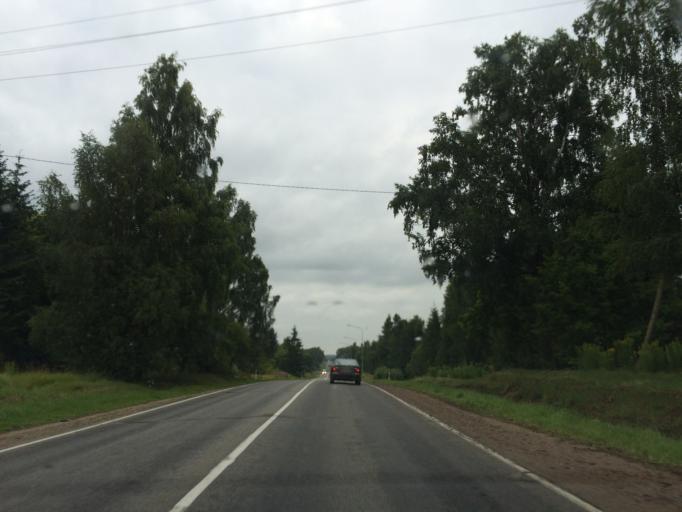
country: LV
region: Rezekne
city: Rezekne
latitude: 56.5397
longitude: 27.3511
